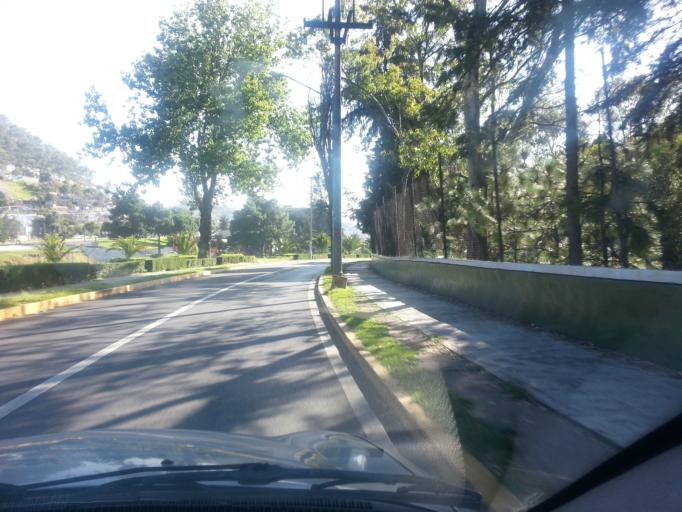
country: MX
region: Mexico
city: San Buenaventura
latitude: 19.2871
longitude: -99.6802
